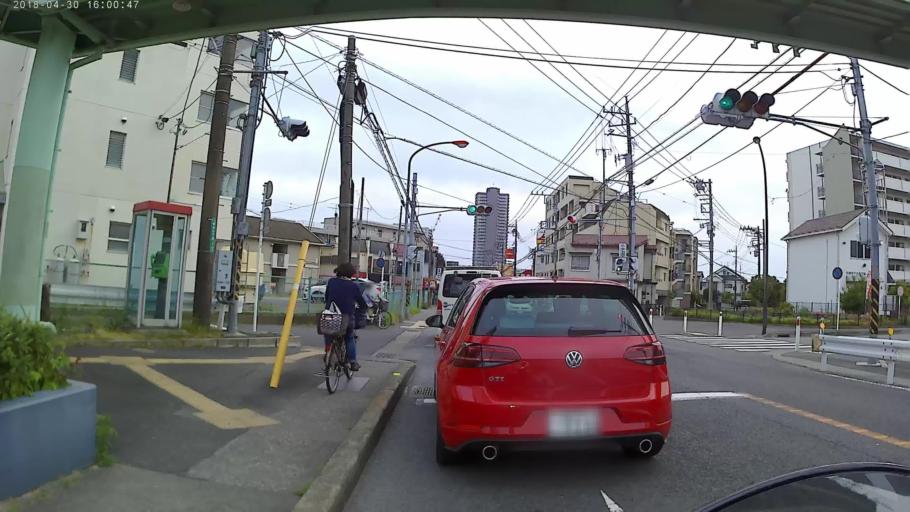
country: JP
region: Tokyo
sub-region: Machida-shi
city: Machida
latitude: 35.5203
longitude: 139.4240
